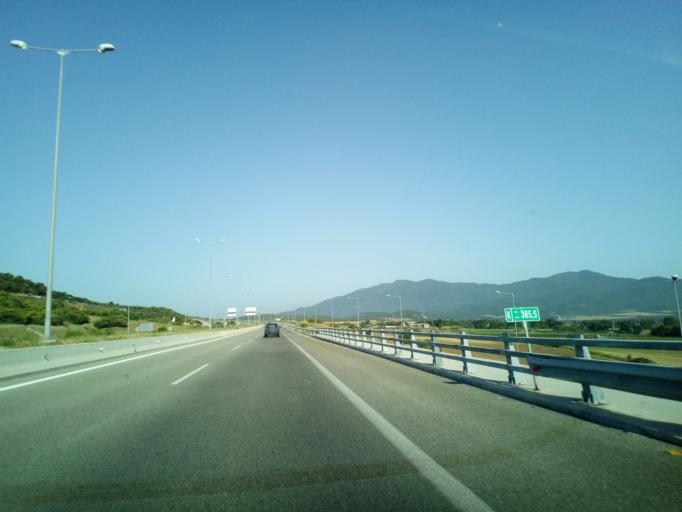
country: GR
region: Central Macedonia
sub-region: Nomos Thessalonikis
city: Stavros
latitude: 40.6765
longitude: 23.5909
